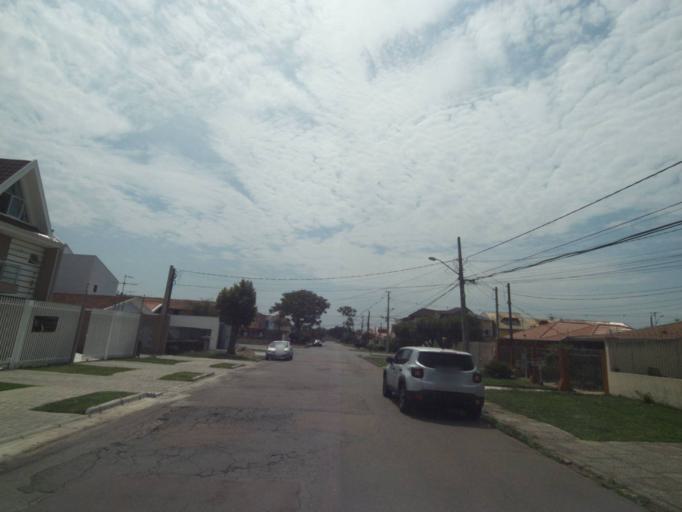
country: BR
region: Parana
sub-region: Pinhais
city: Pinhais
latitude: -25.4247
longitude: -49.2012
